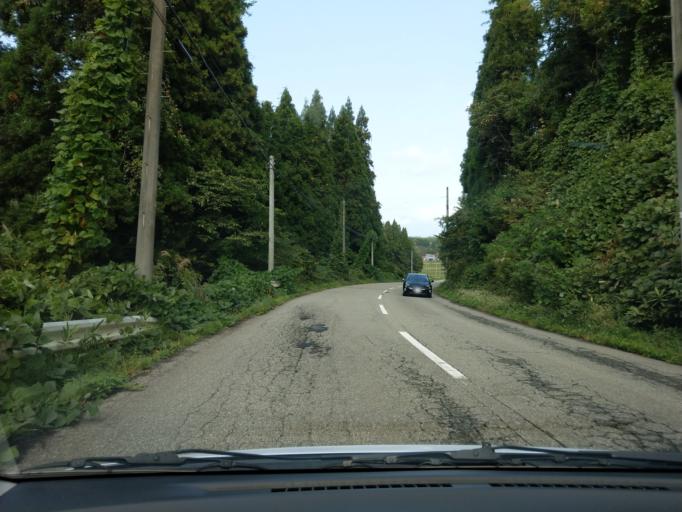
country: JP
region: Akita
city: Omagari
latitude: 39.5130
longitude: 140.3070
